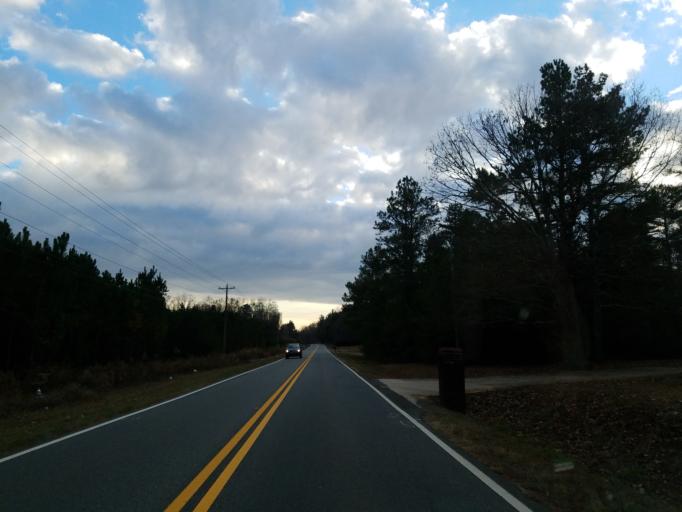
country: US
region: Georgia
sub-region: Dawson County
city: Dawsonville
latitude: 34.3189
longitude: -84.0772
